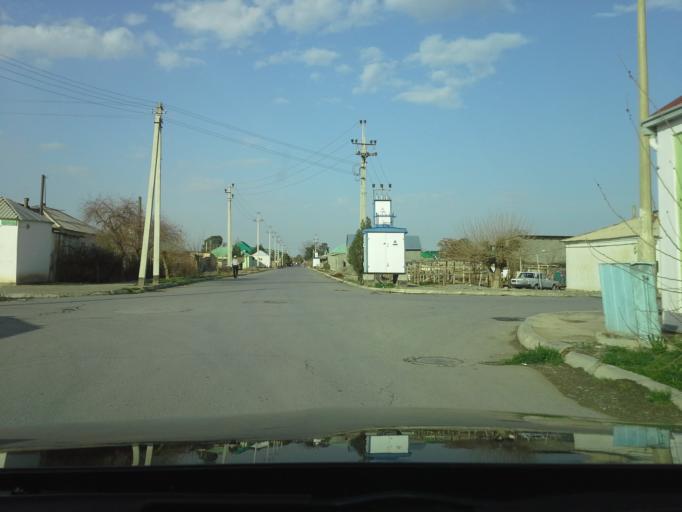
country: TM
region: Ahal
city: Abadan
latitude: 38.0228
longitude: 58.2334
